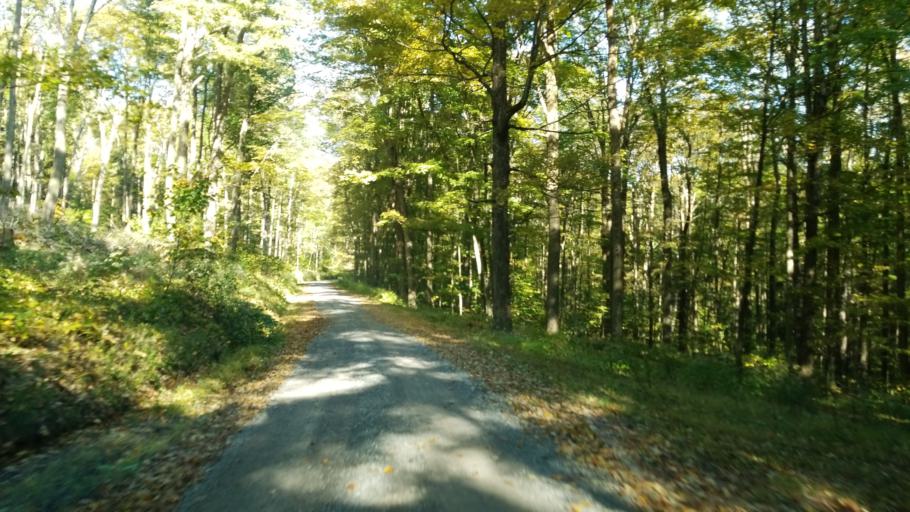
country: US
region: Pennsylvania
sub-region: Clearfield County
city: Treasure Lake
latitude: 41.1412
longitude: -78.5735
